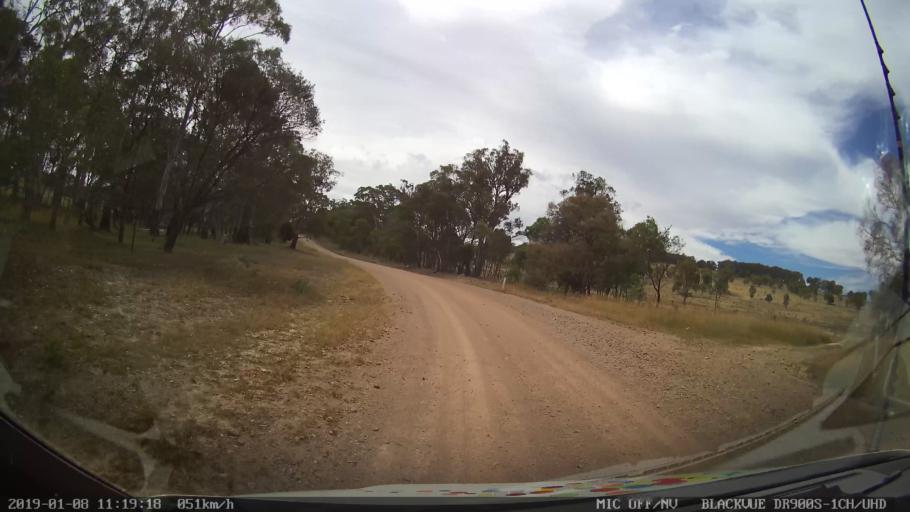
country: AU
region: New South Wales
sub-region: Guyra
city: Guyra
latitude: -30.2271
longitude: 151.5524
